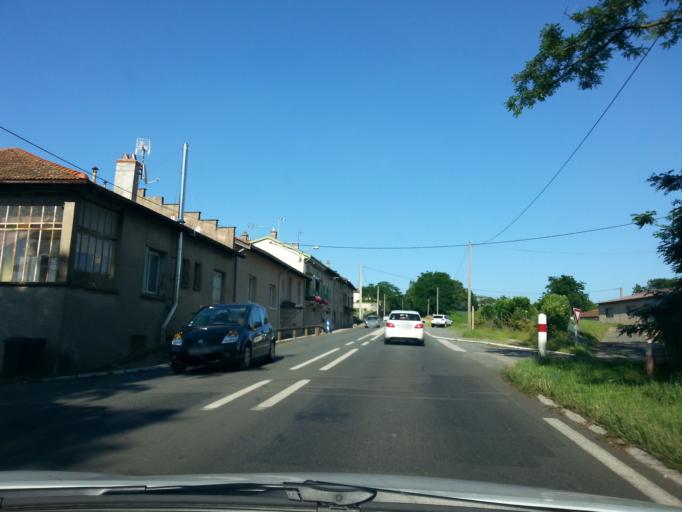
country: FR
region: Rhone-Alpes
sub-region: Departement du Rhone
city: Charentay
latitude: 46.1200
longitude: 4.6839
